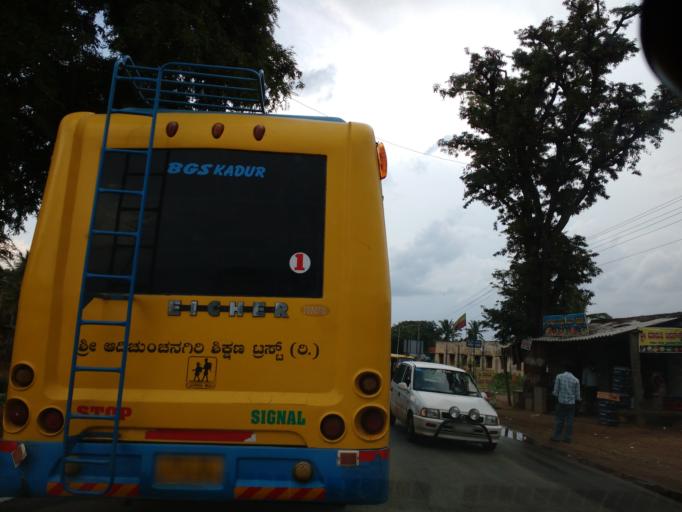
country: IN
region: Karnataka
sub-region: Chikmagalur
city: Kadur
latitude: 13.5278
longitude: 76.0333
